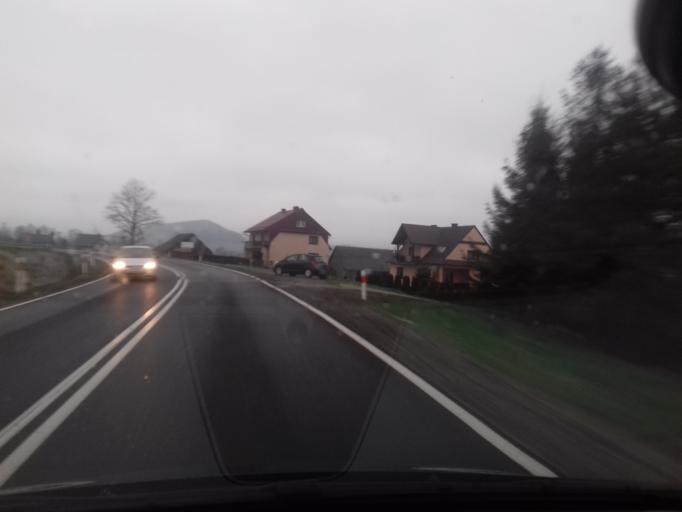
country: PL
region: Lesser Poland Voivodeship
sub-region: Powiat limanowski
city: Tymbark
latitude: 49.7285
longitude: 20.2939
